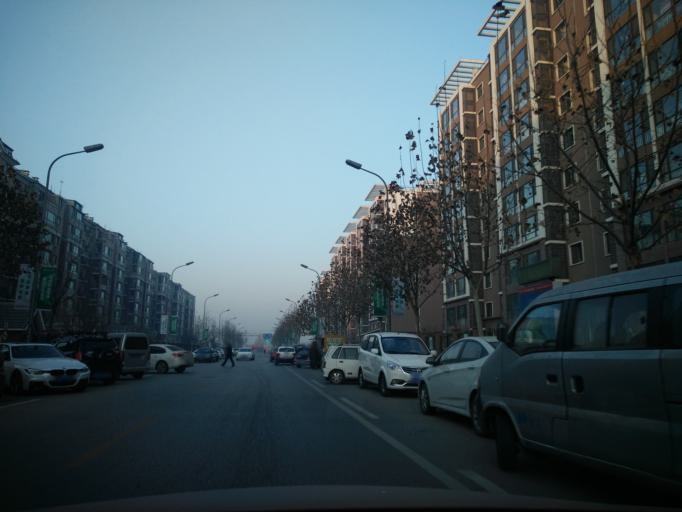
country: CN
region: Beijing
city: Yinghai
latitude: 39.7149
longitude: 116.3945
